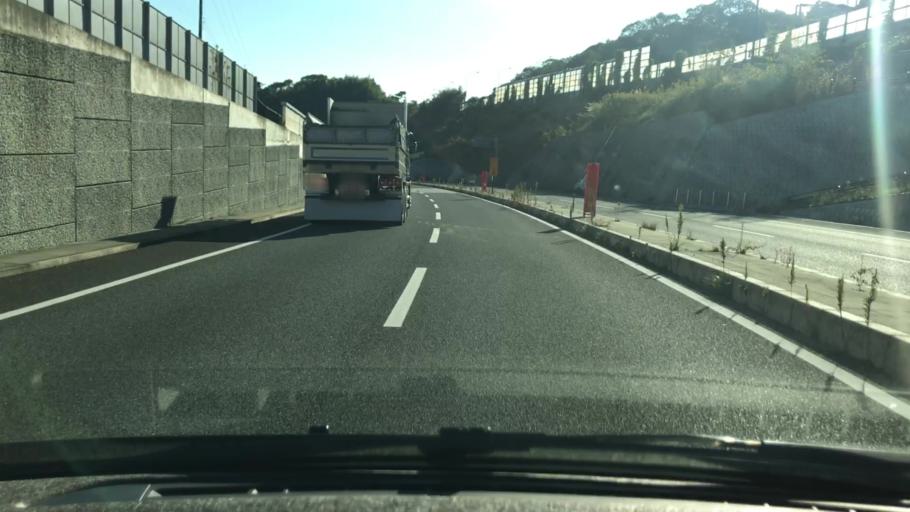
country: JP
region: Hyogo
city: Takarazuka
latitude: 34.8285
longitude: 135.2976
